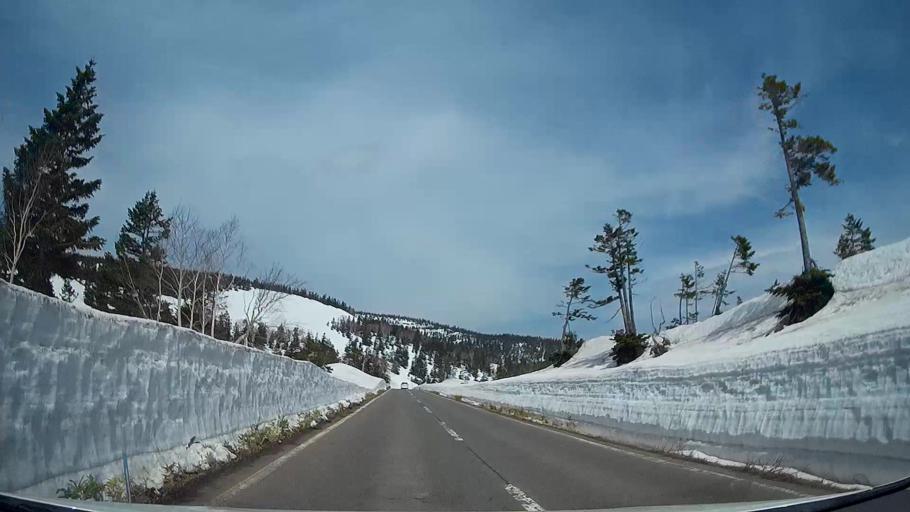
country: JP
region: Akita
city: Hanawa
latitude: 39.9534
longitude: 140.8870
